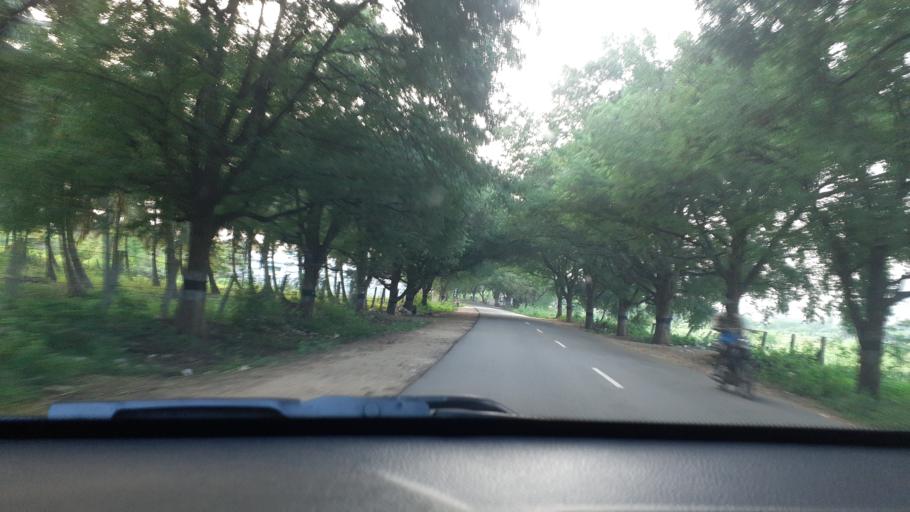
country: IN
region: Tamil Nadu
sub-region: Dindigul
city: Palani
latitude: 10.4290
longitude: 77.5291
